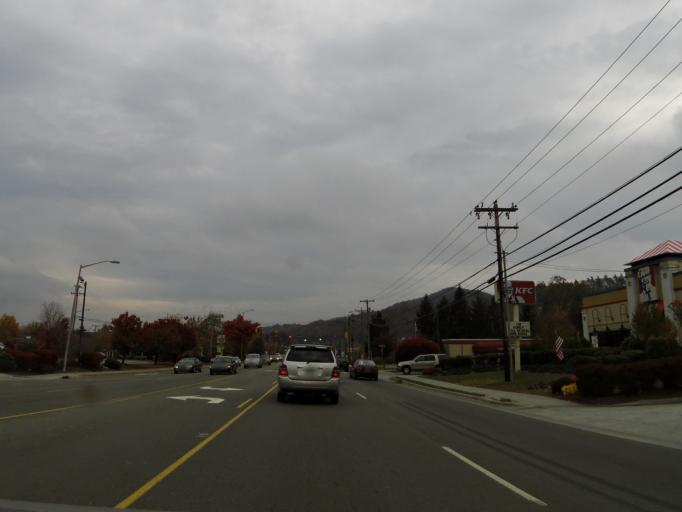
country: US
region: North Carolina
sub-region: Watauga County
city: Boone
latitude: 36.2002
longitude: -81.6603
